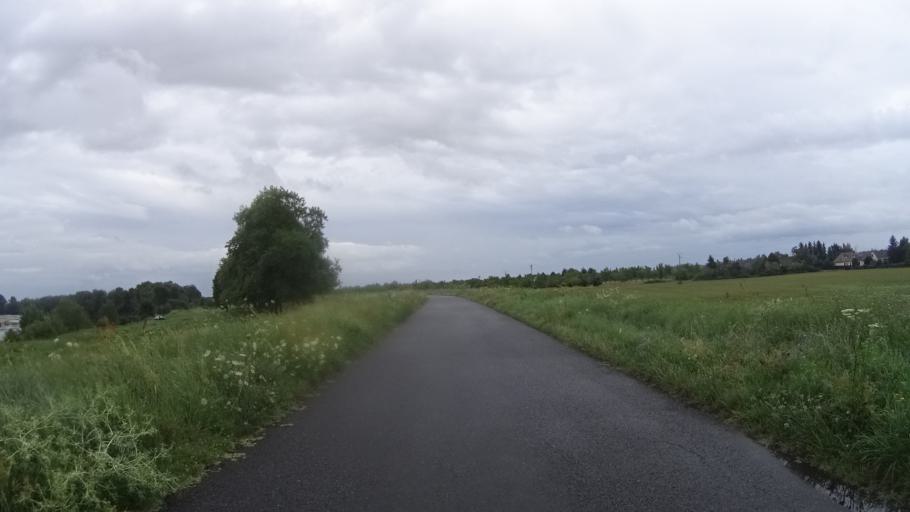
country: FR
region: Centre
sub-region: Departement du Loiret
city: Sandillon
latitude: 47.8531
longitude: 2.0381
